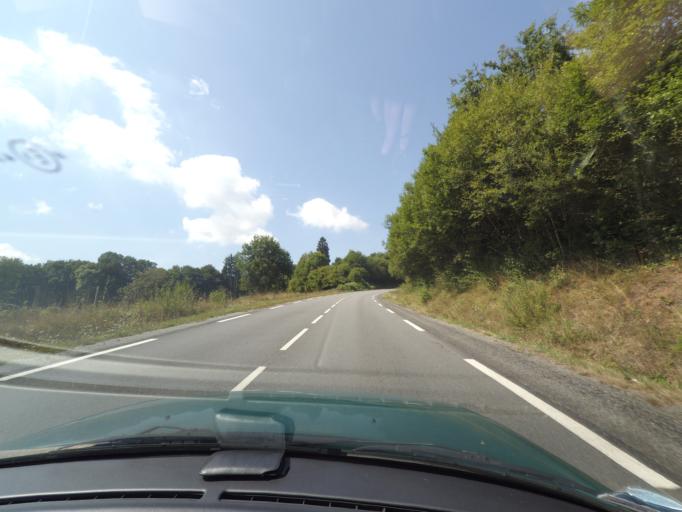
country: FR
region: Limousin
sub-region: Departement de la Haute-Vienne
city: Linards
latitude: 45.7658
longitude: 1.5440
